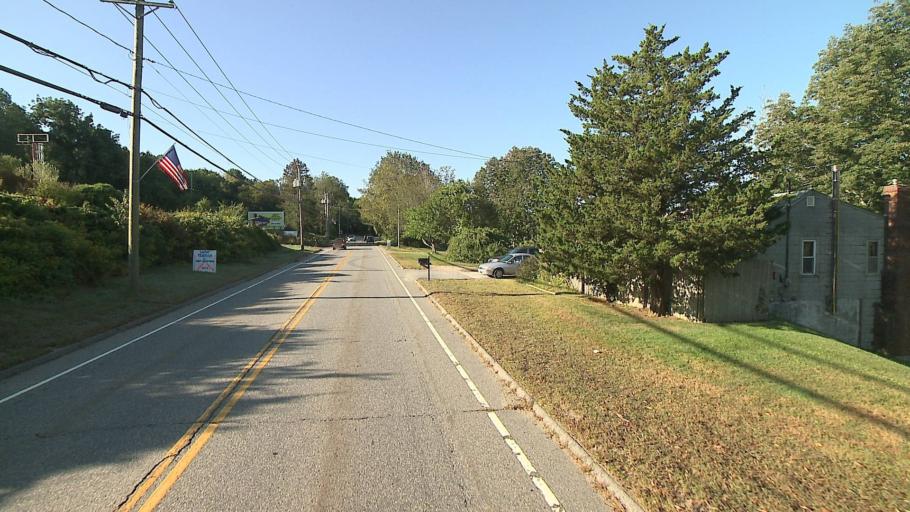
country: US
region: Connecticut
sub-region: Windham County
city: Moosup
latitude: 41.7036
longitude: -71.9059
